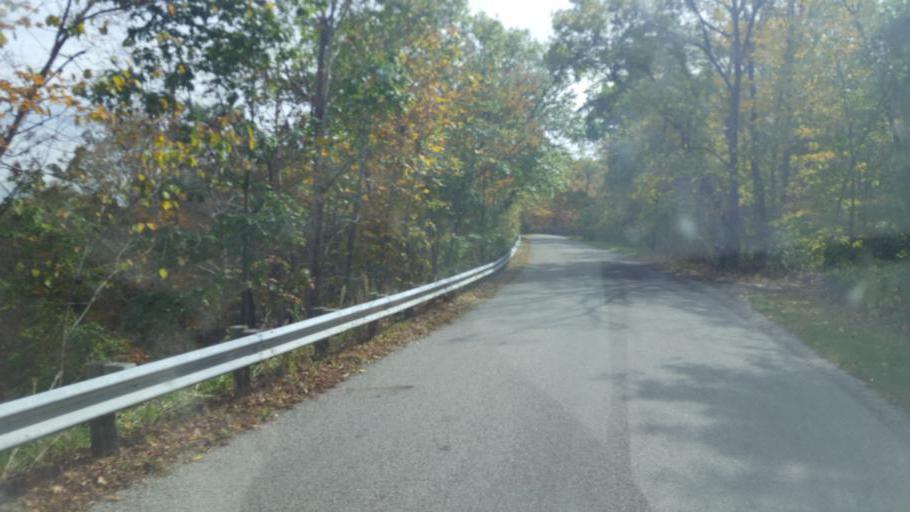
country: US
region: Ohio
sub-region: Lorain County
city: Vermilion-on-the-Lake
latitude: 41.3892
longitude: -82.3307
